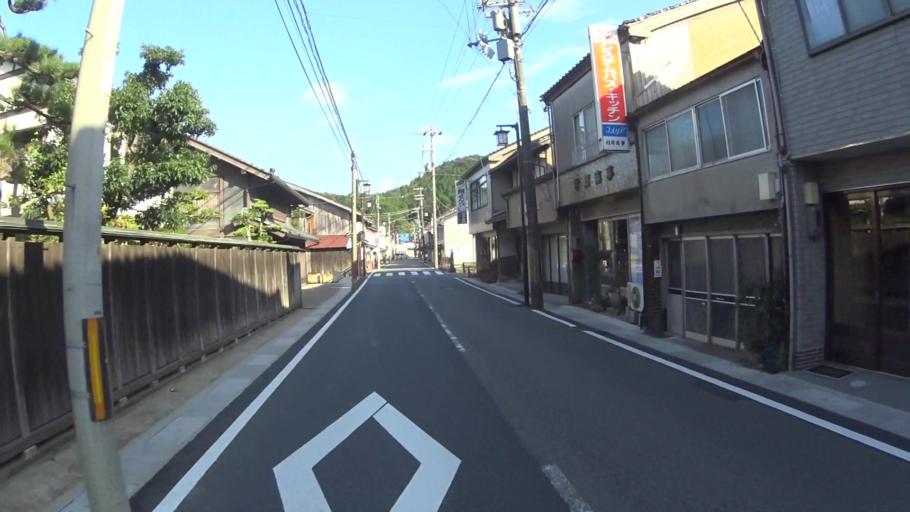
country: JP
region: Hyogo
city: Toyooka
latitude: 35.6058
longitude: 134.8988
